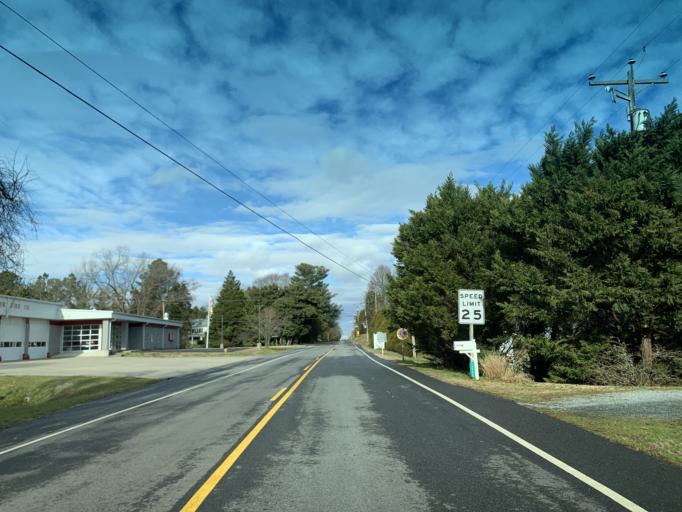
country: US
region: Maryland
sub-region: Harford County
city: Aberdeen Proving Ground
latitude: 39.3620
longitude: -76.0625
